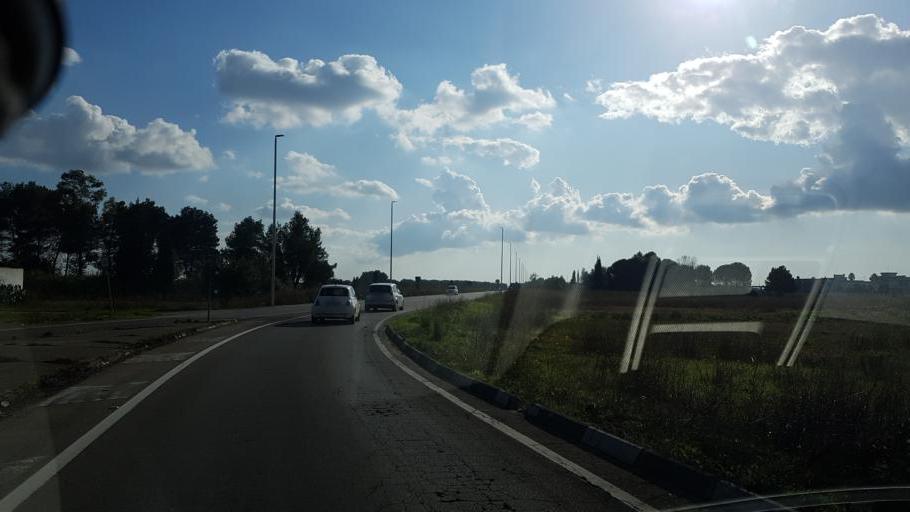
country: IT
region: Apulia
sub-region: Provincia di Lecce
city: Salice Salentino
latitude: 40.3804
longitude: 17.9698
